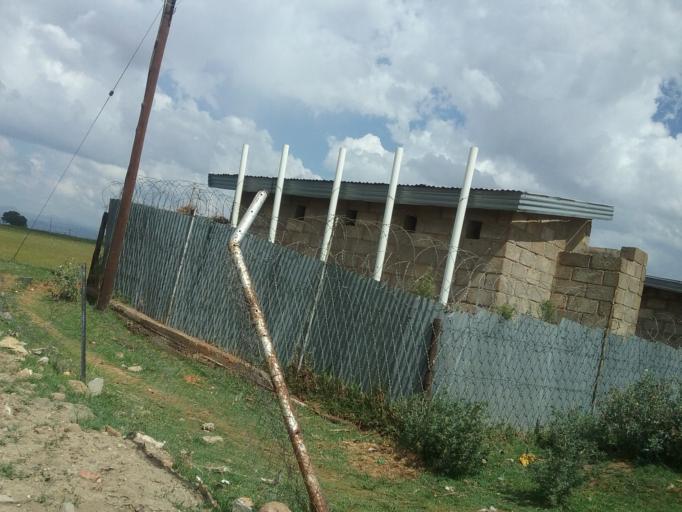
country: LS
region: Maseru
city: Maseru
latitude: -29.4215
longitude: 27.5650
